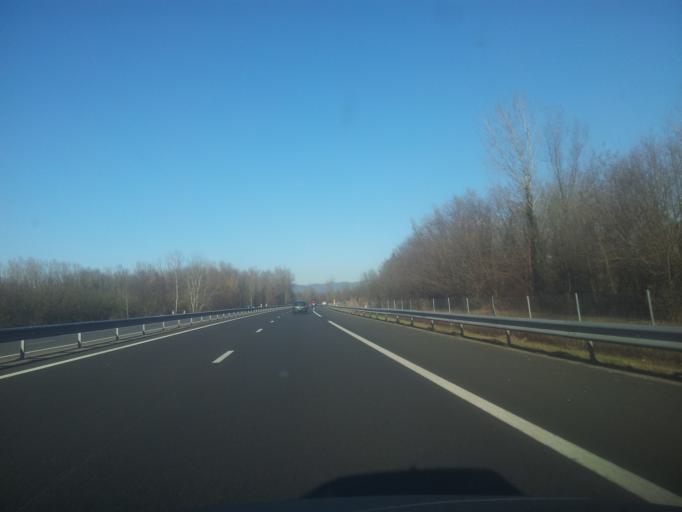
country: FR
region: Rhone-Alpes
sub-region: Departement de l'Isere
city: Saint-Quentin-sur-Isere
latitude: 45.2485
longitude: 5.5036
